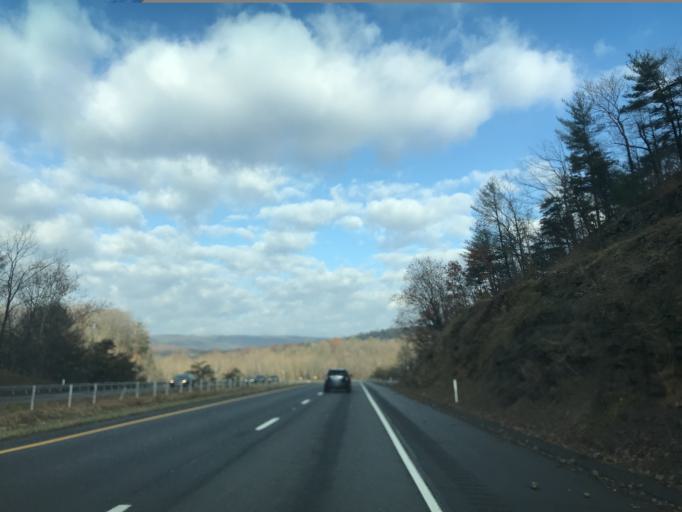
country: US
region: Maryland
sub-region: Washington County
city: Hancock
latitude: 39.7790
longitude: -78.2024
